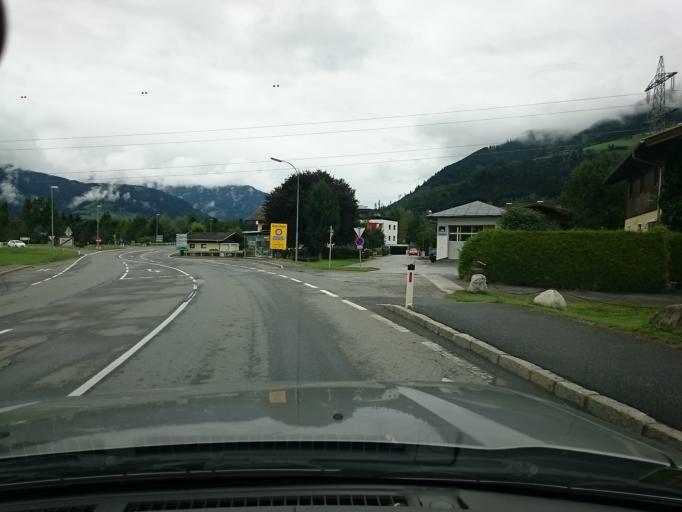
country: AT
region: Salzburg
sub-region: Politischer Bezirk Zell am See
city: Bruck an der Grossglocknerstrasse
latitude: 47.2783
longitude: 12.8261
